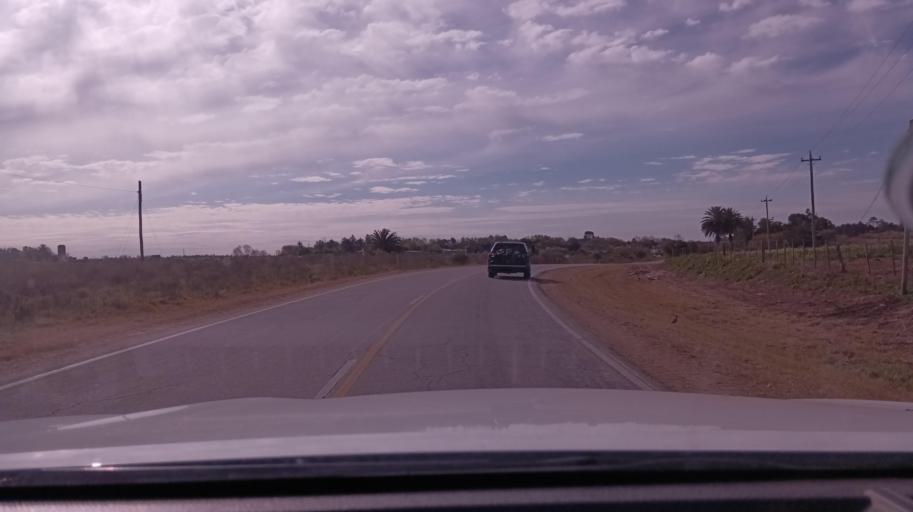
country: UY
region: Canelones
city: Toledo
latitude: -34.7163
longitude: -56.1133
